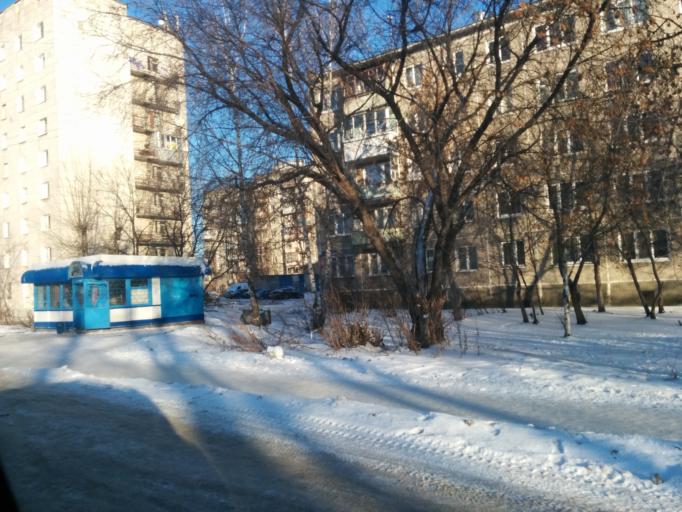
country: RU
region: Perm
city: Overyata
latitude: 58.0109
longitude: 55.9270
